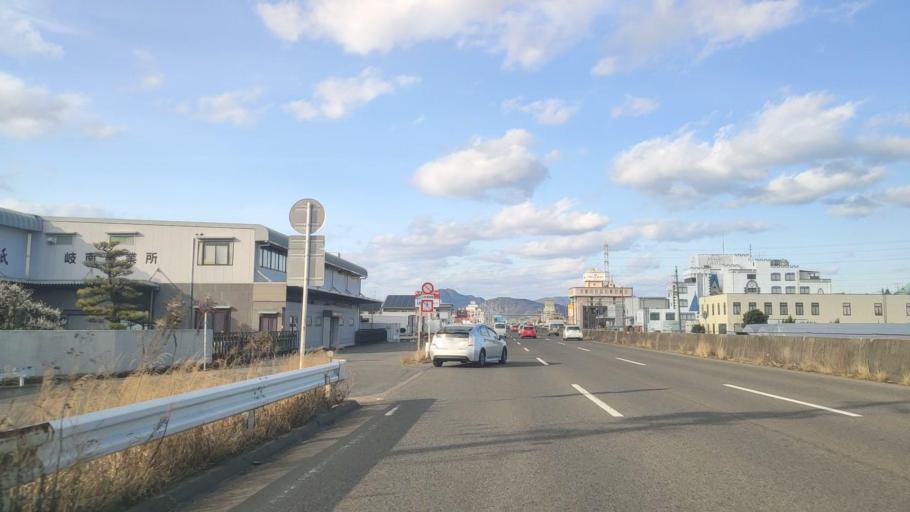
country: JP
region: Gifu
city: Kasamatsucho
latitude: 35.3775
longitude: 136.7841
